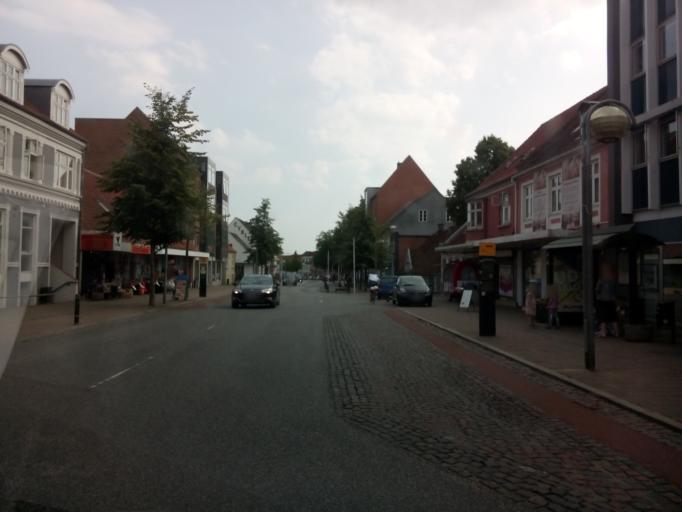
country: DK
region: Central Jutland
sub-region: Skanderborg Kommune
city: Skanderborg
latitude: 56.0332
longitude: 9.9321
